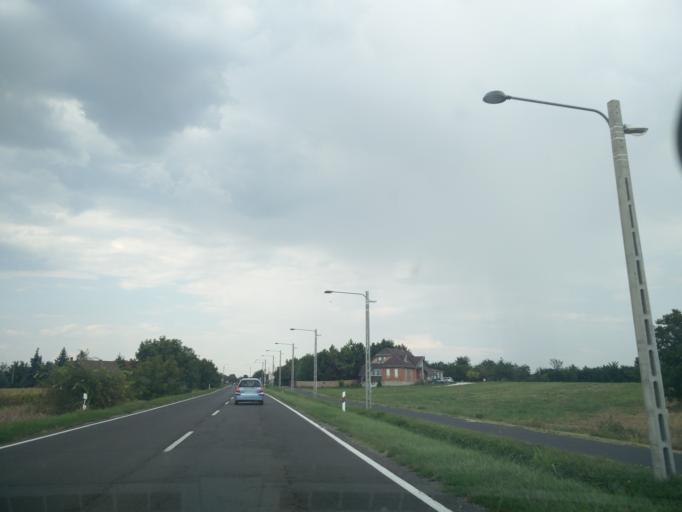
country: HU
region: Fejer
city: Polgardi
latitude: 47.0560
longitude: 18.3061
